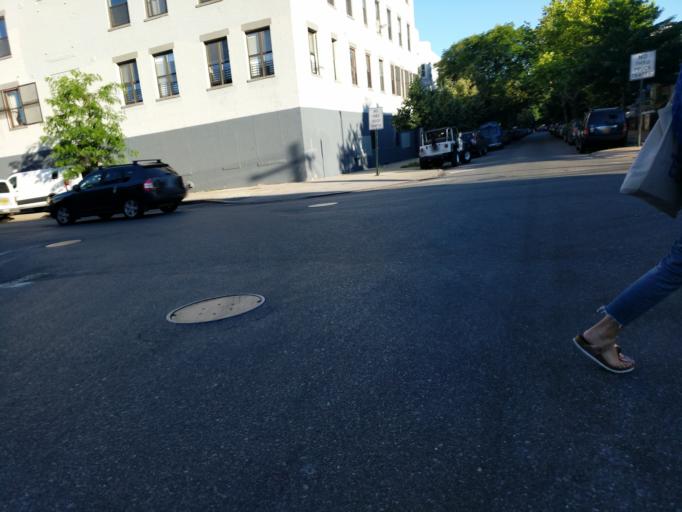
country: US
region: New York
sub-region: Queens County
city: Long Island City
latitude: 40.7278
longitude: -73.9430
